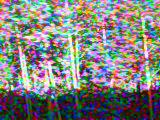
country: SE
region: Soedermanland
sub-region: Flens Kommun
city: Flen
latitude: 59.0757
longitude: 16.5965
